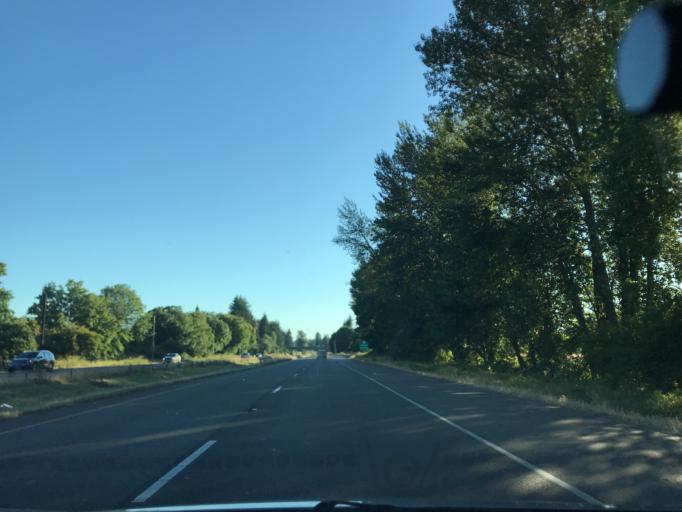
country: US
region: Washington
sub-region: Pierce County
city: Sumner
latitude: 47.1946
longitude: -122.2225
